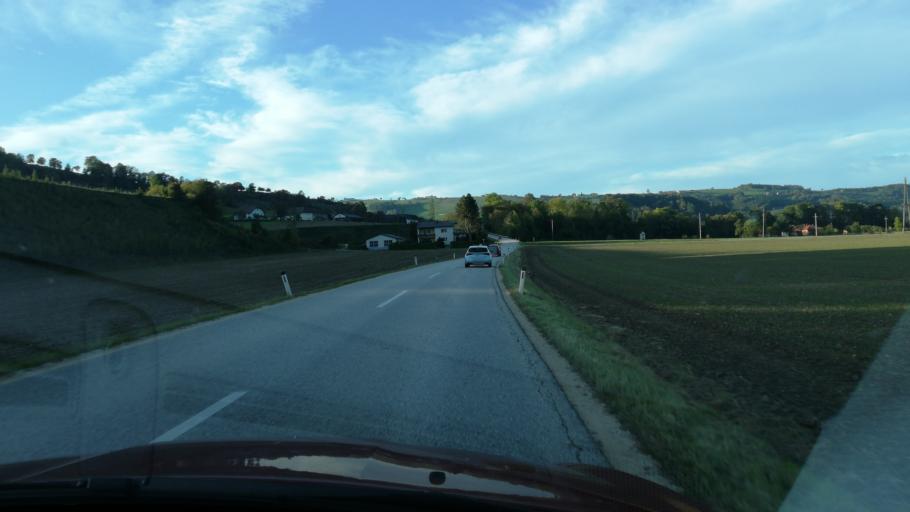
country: AT
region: Upper Austria
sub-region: Politischer Bezirk Steyr-Land
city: Ternberg
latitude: 47.9608
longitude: 14.3486
